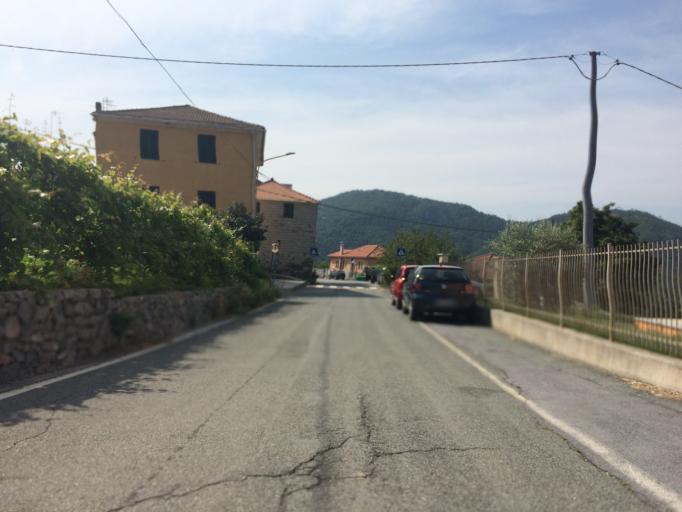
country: IT
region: Liguria
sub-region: Provincia di Savona
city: San Giovanni
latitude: 44.3910
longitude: 8.5249
